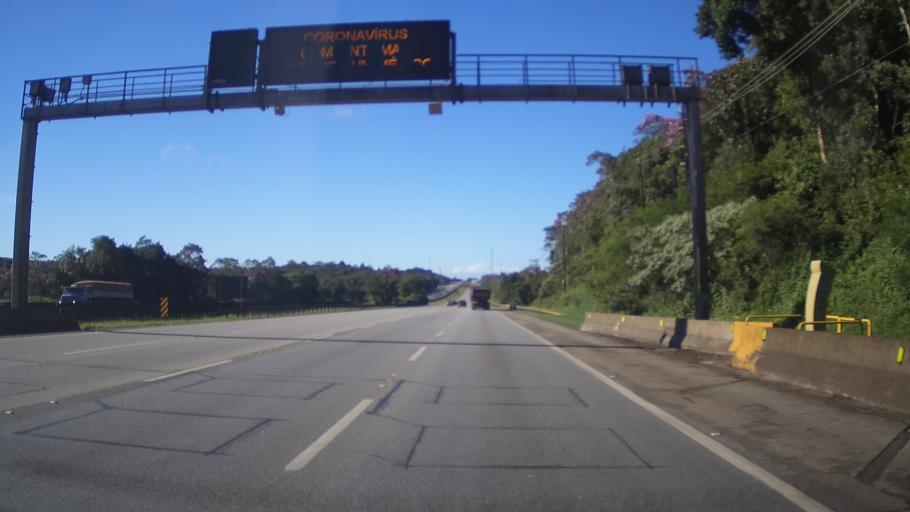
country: BR
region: Sao Paulo
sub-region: Cubatao
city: Cubatao
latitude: -23.8707
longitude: -46.5719
